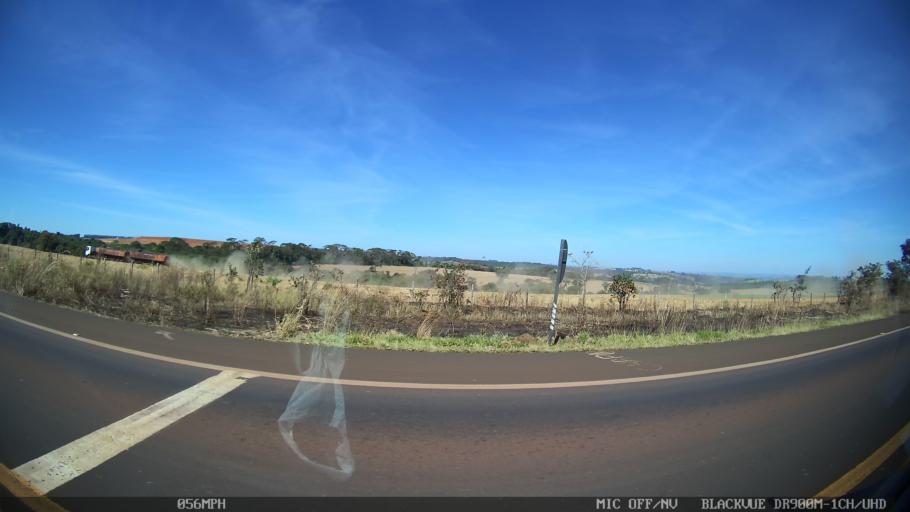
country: BR
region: Sao Paulo
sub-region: Franca
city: Franca
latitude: -20.5489
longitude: -47.4822
